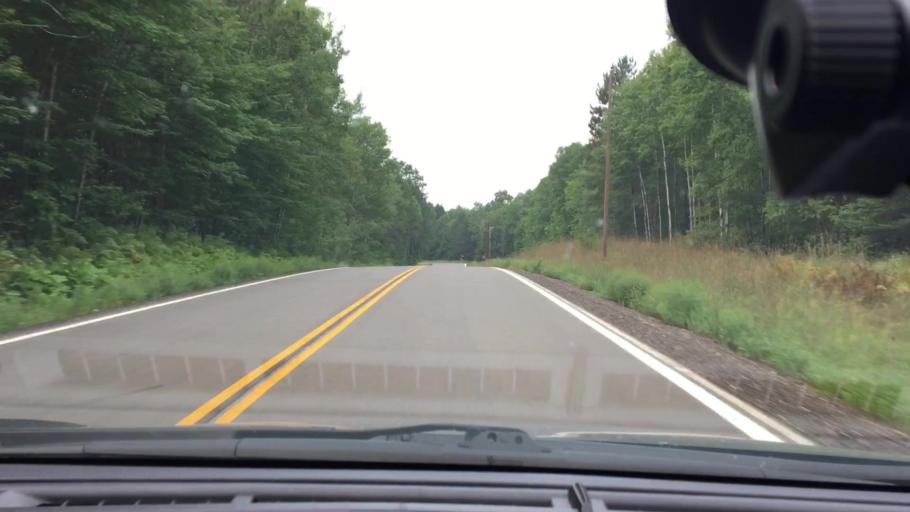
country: US
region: Minnesota
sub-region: Crow Wing County
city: Cross Lake
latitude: 46.6590
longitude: -93.9714
